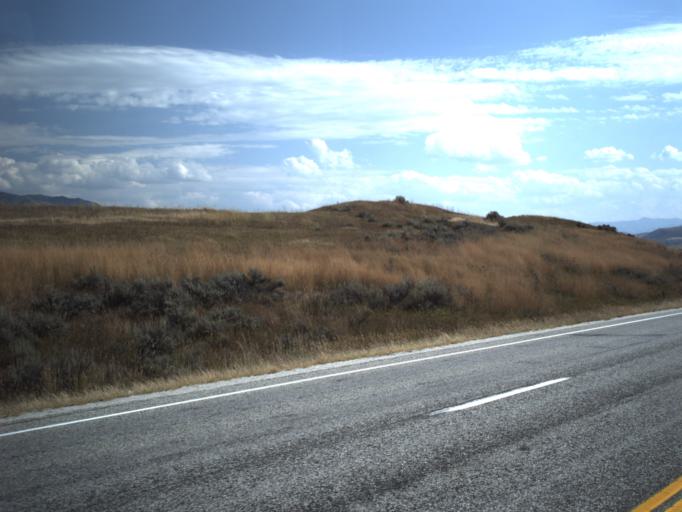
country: US
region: Utah
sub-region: Morgan County
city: Mountain Green
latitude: 41.1561
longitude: -111.7972
